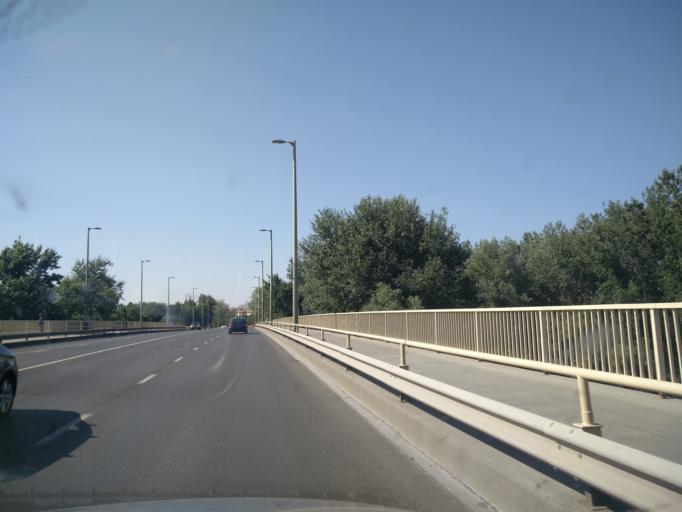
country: HU
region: Csongrad
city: Szeged
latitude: 46.2564
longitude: 20.1650
